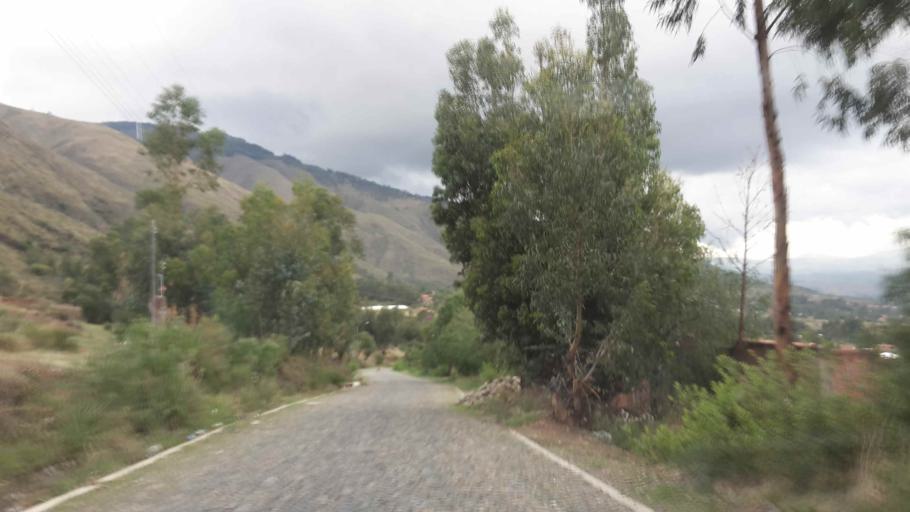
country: BO
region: Cochabamba
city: Cochabamba
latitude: -17.3736
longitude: -66.0581
